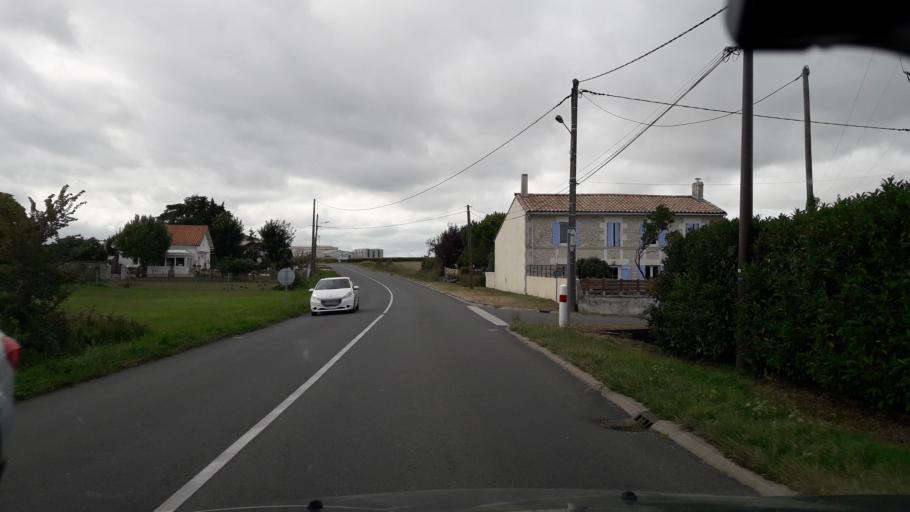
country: FR
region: Poitou-Charentes
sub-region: Departement de la Charente-Maritime
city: Saint-Sulpice-de-Royan
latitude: 45.6809
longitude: -0.9918
